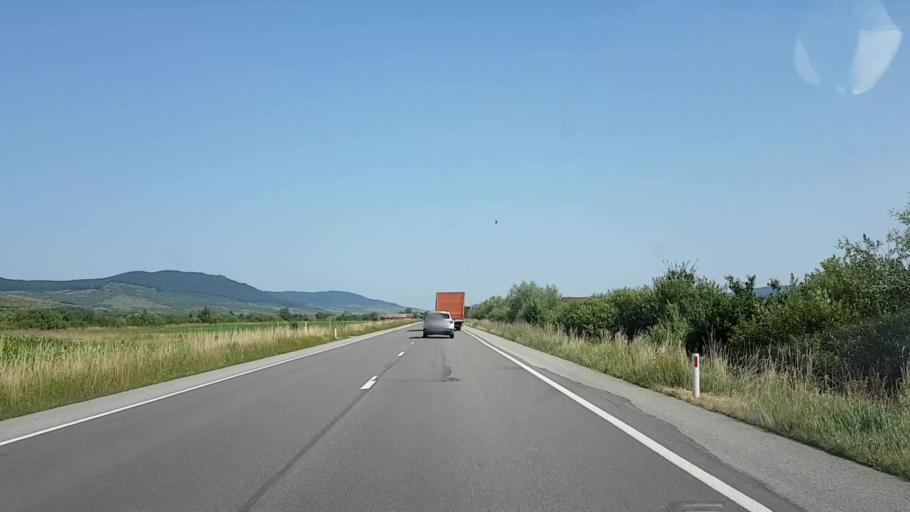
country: RO
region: Bistrita-Nasaud
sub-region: Comuna Sieu-Odorhei
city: Sieu-Odorhei
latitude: 47.1213
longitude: 24.3269
